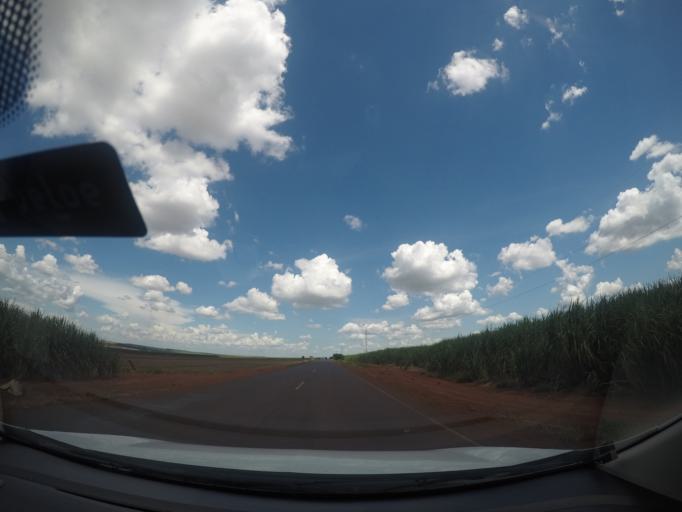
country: BR
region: Minas Gerais
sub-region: Frutal
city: Frutal
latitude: -19.8577
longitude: -48.7330
